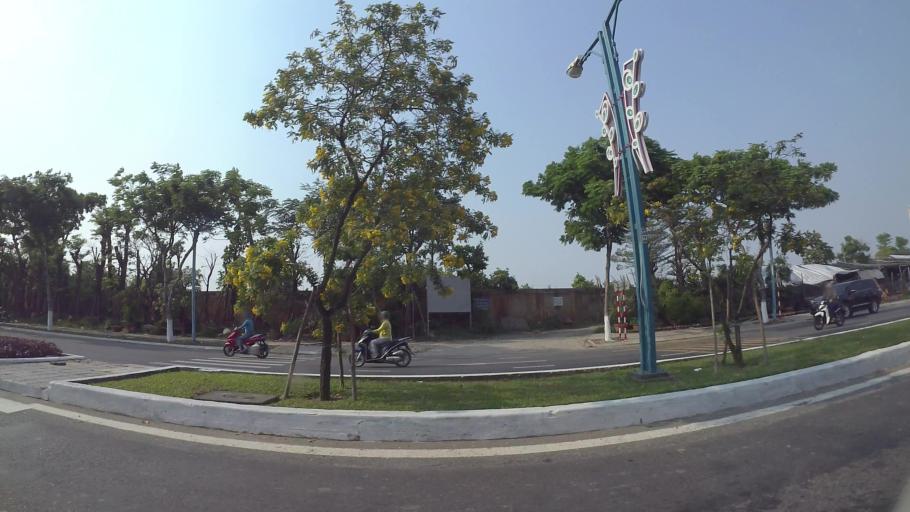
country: VN
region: Da Nang
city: Cam Le
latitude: 16.0238
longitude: 108.2063
